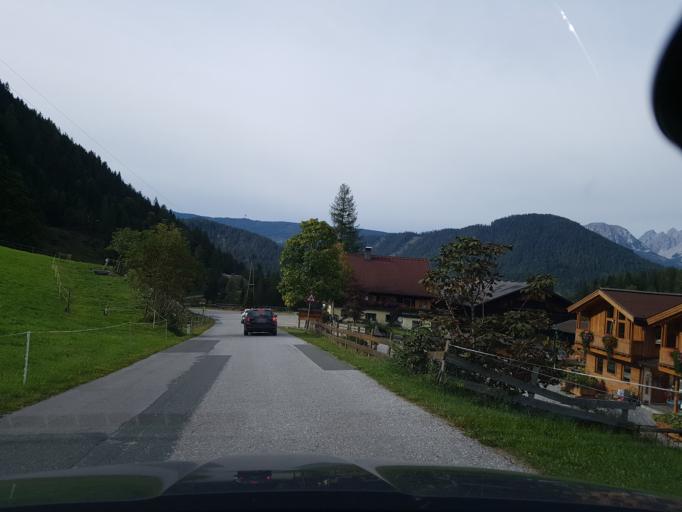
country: AT
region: Salzburg
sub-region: Politischer Bezirk Sankt Johann im Pongau
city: Forstau
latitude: 47.3650
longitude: 13.5569
